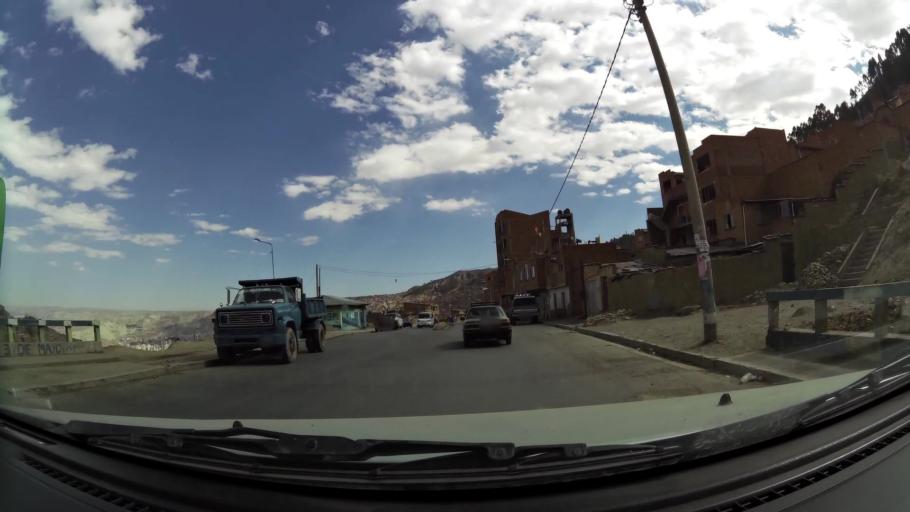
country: BO
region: La Paz
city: La Paz
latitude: -16.4643
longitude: -68.1131
